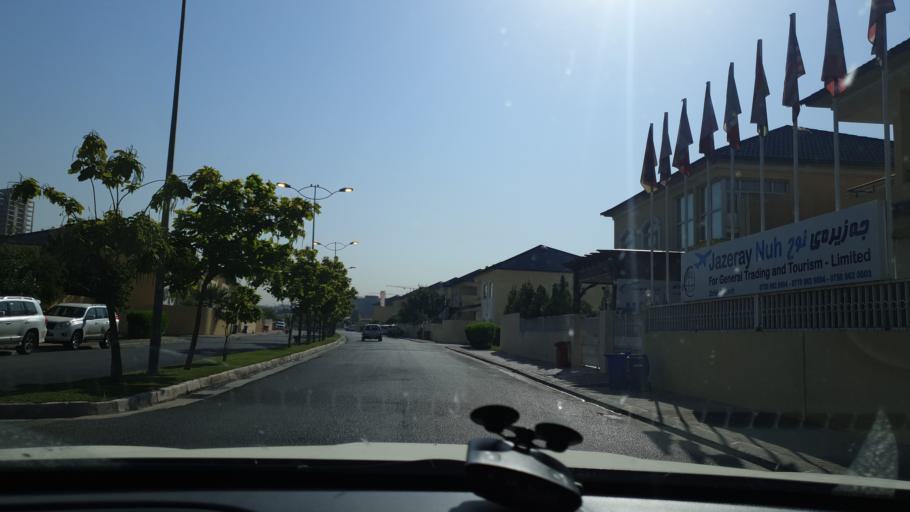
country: IQ
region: Arbil
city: Erbil
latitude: 36.1872
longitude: 43.9659
